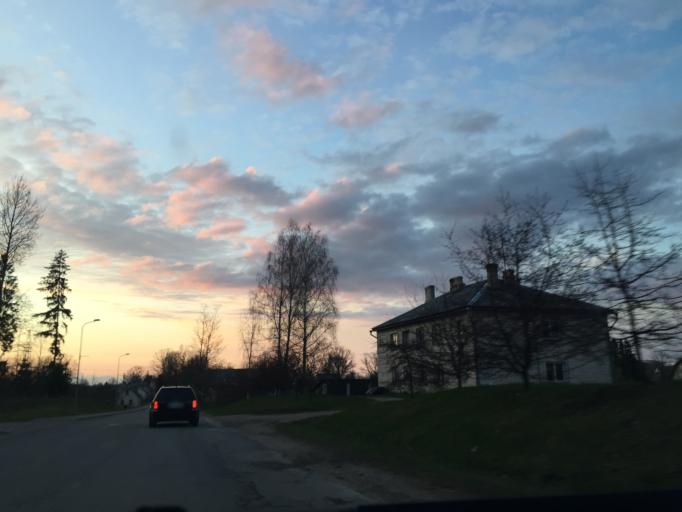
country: LV
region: Aluksnes Rajons
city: Aluksne
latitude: 57.4089
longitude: 27.0443
